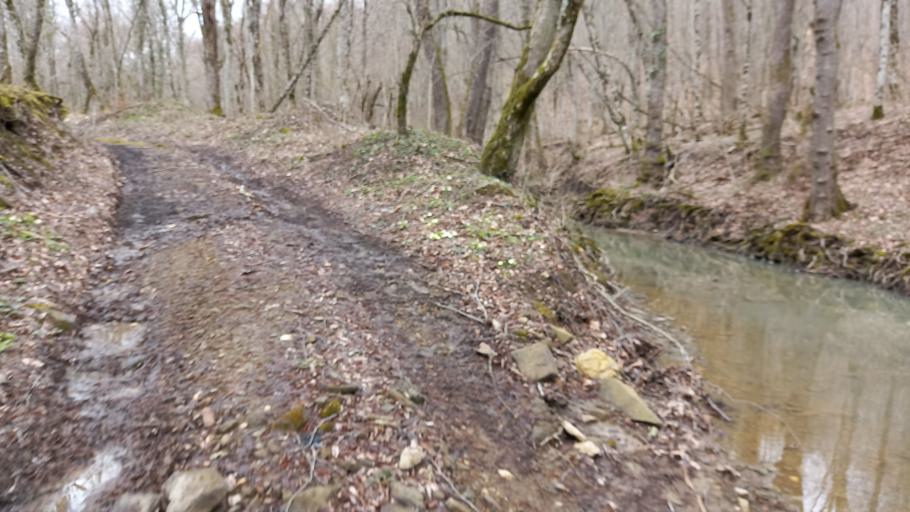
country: RU
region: Krasnodarskiy
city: Pshada
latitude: 44.4913
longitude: 38.3910
